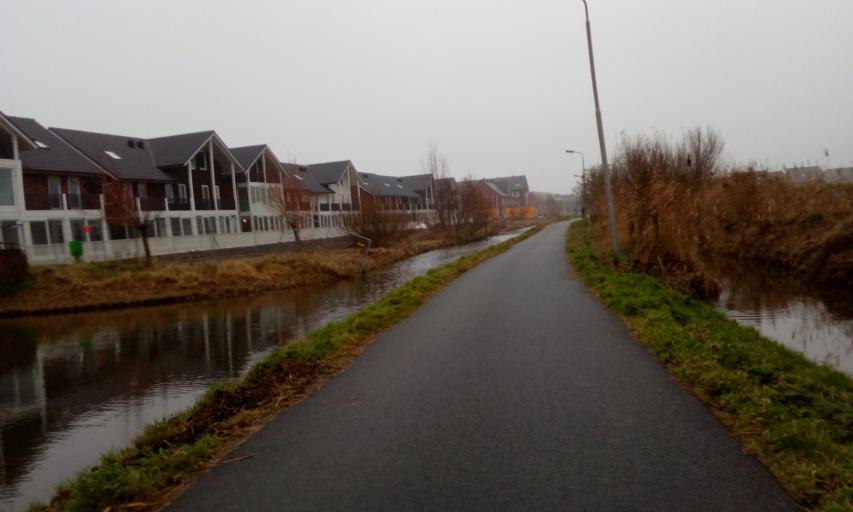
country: NL
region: South Holland
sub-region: Gemeente Pijnacker-Nootdorp
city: Pijnacker
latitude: 52.0054
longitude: 4.4388
